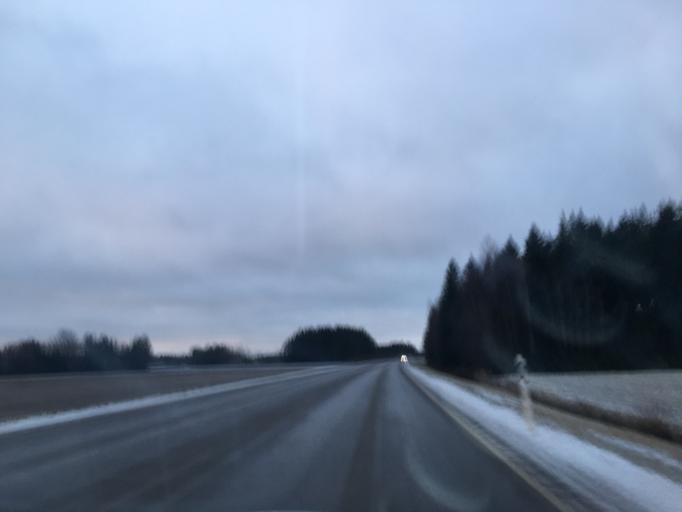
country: FI
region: Varsinais-Suomi
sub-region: Loimaa
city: Aura
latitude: 60.6600
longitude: 22.5590
